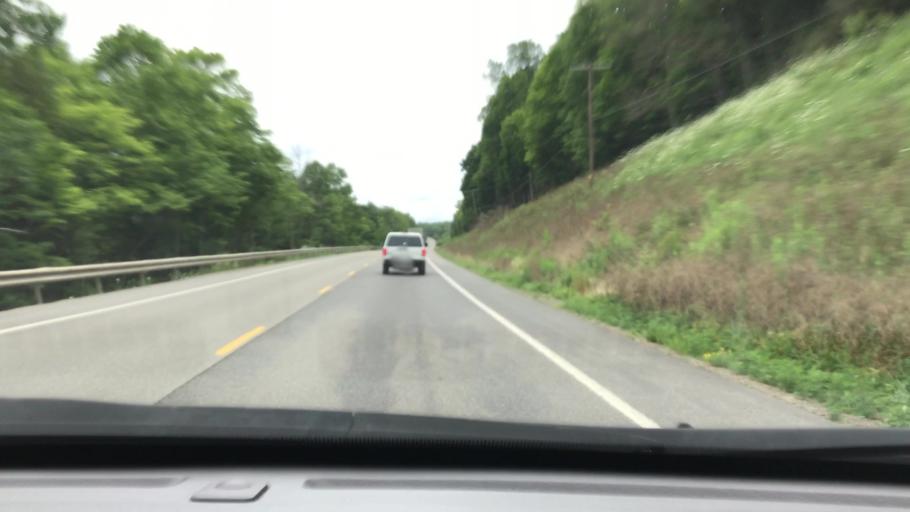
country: US
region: Pennsylvania
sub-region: McKean County
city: Kane
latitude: 41.6884
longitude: -78.6898
